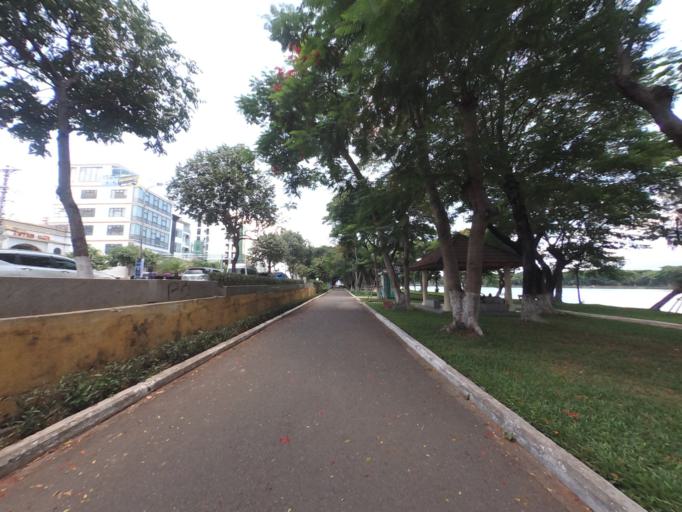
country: VN
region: Da Nang
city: Da Nang
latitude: 16.0605
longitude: 108.2055
